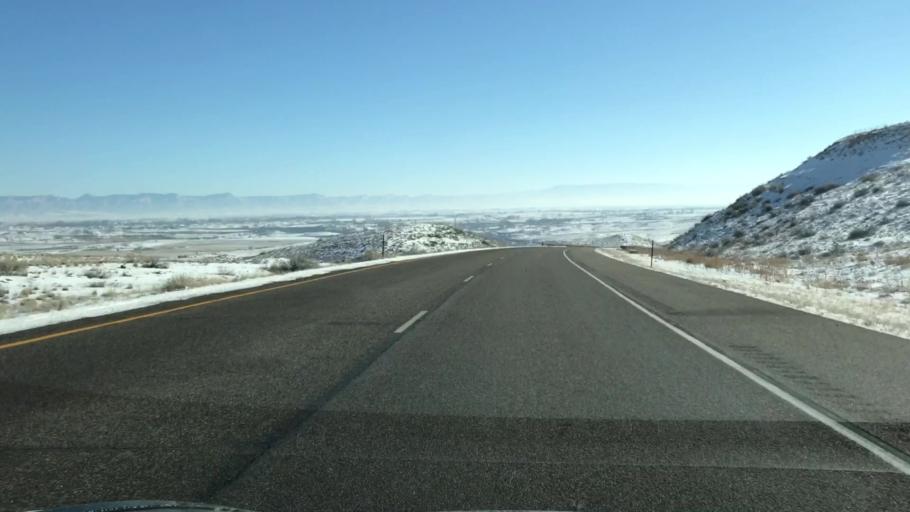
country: US
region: Colorado
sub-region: Mesa County
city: Loma
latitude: 39.2296
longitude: -108.9071
